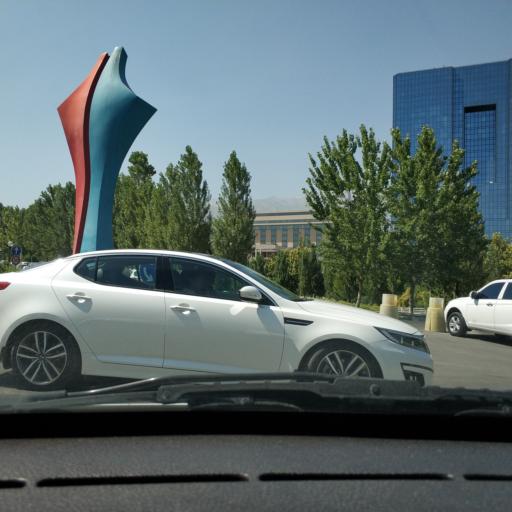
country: IR
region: Tehran
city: Tajrish
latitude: 35.7559
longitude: 51.4344
